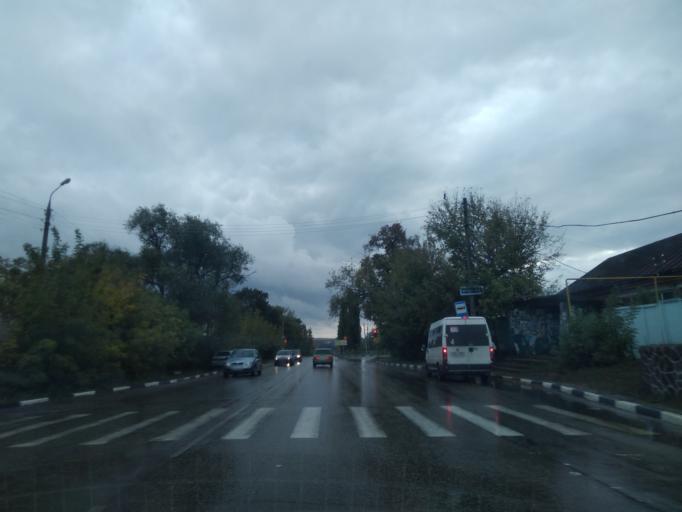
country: RU
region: Tula
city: Yefremov
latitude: 53.1335
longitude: 38.1175
